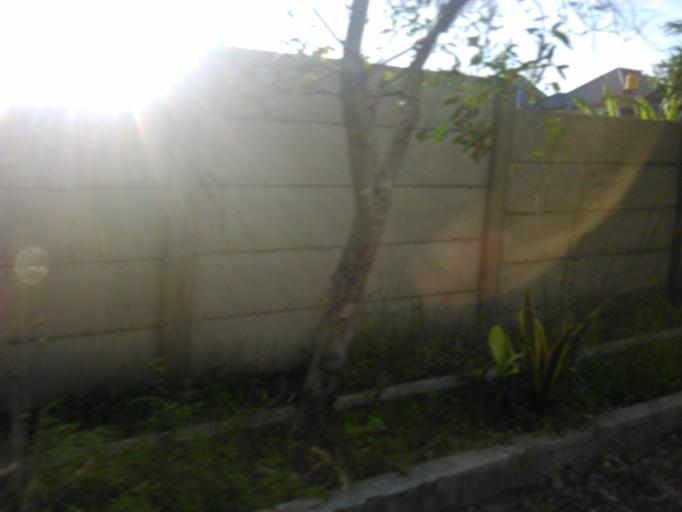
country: ID
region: East Java
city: Wonorejo
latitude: -7.2905
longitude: 112.8035
